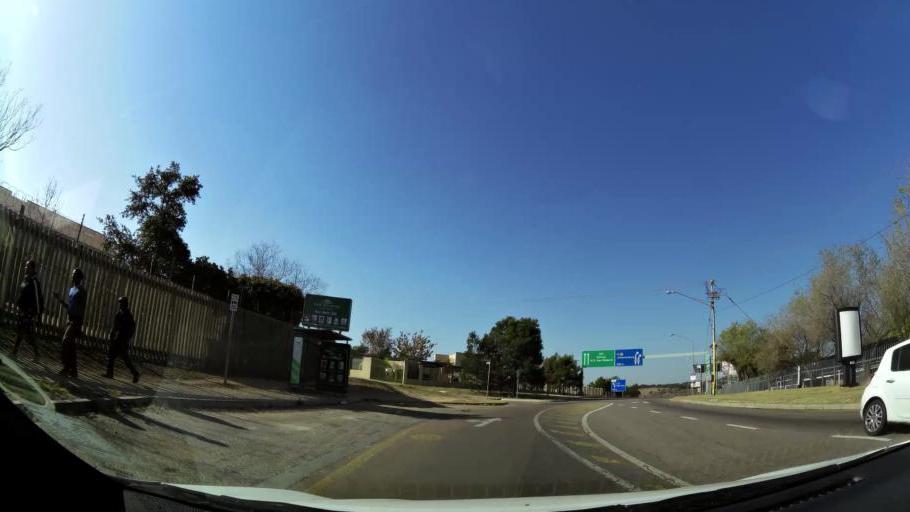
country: ZA
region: Gauteng
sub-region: City of Tshwane Metropolitan Municipality
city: Centurion
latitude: -25.8082
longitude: 28.2556
